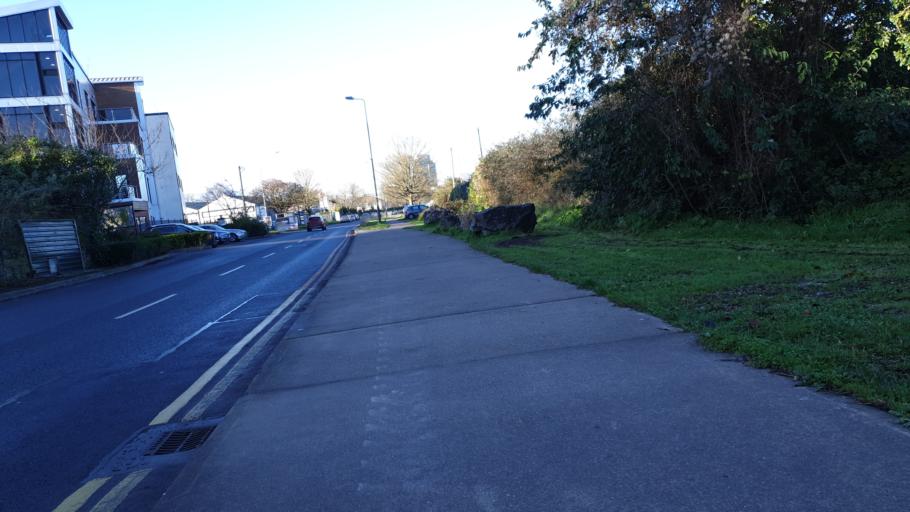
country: IE
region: Munster
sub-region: County Cork
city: Cork
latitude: 51.8954
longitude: -8.4498
